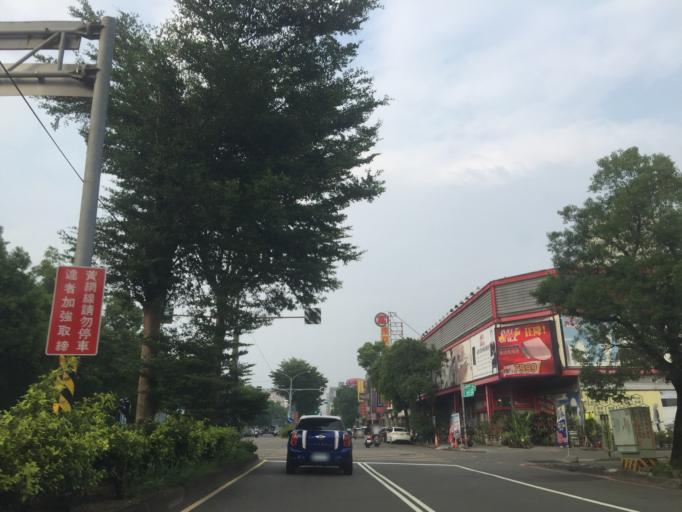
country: TW
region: Taiwan
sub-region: Hsinchu
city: Zhubei
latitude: 24.8256
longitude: 121.0154
